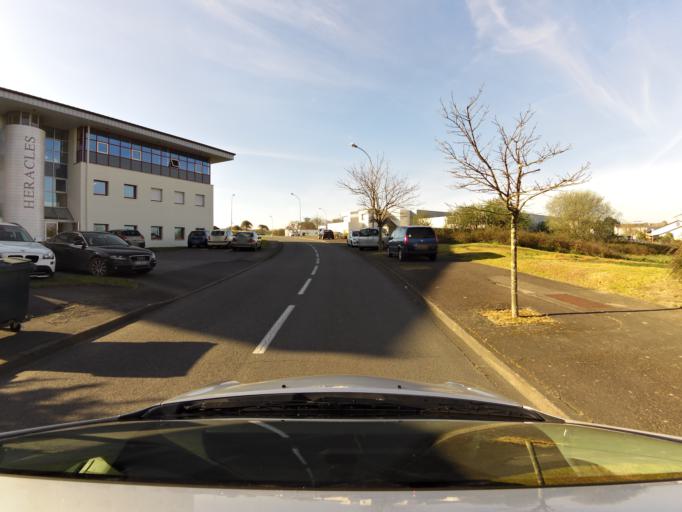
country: FR
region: Brittany
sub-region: Departement du Morbihan
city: Larmor-Plage
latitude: 47.7259
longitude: -3.3862
